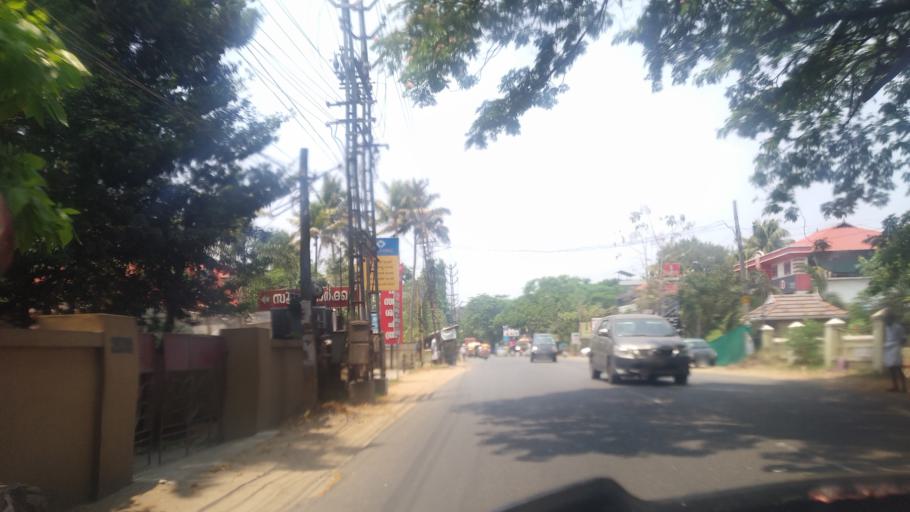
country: IN
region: Kerala
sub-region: Thrissur District
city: Kodungallur
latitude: 10.2347
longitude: 76.1943
